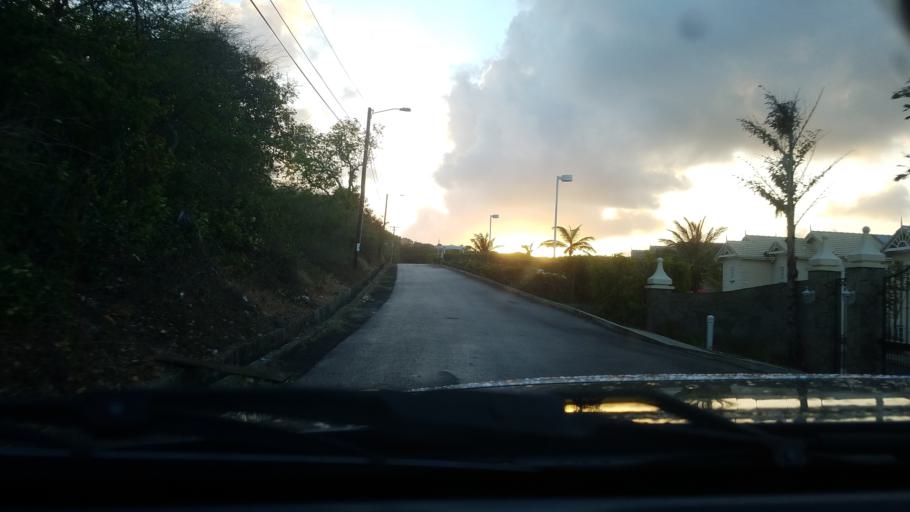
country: LC
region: Gros-Islet
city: Gros Islet
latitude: 14.0897
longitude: -60.9339
